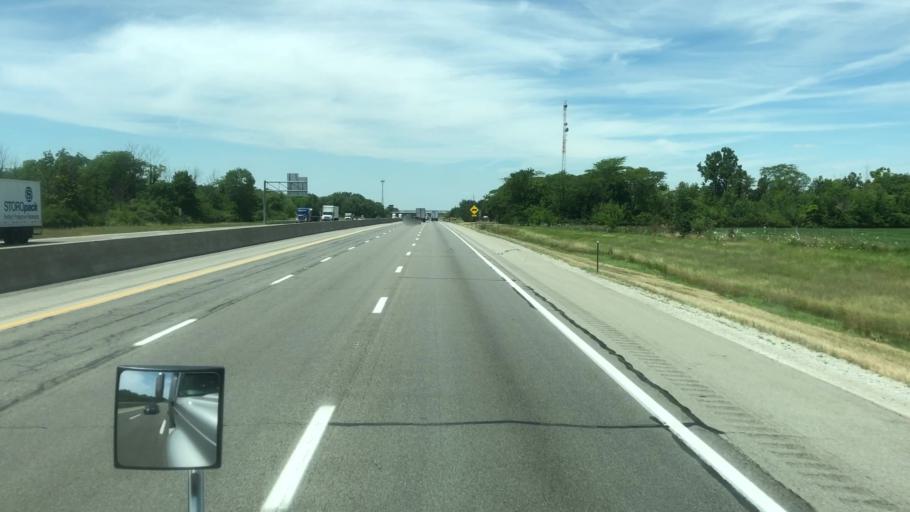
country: US
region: Ohio
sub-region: Ottawa County
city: Elmore
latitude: 41.4694
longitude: -83.3155
